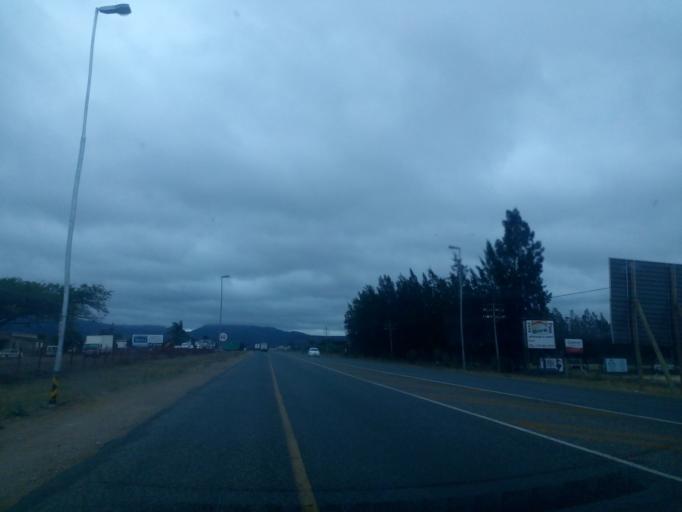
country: ZA
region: Limpopo
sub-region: Vhembe District Municipality
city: Louis Trichardt
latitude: -23.0765
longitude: 29.9092
